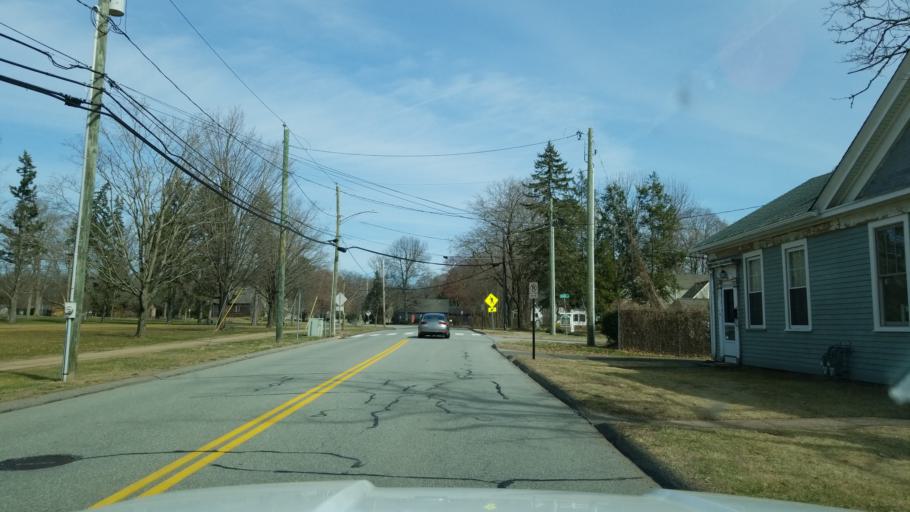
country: US
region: Connecticut
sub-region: Hartford County
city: Glastonbury Center
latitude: 41.7006
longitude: -72.6056
